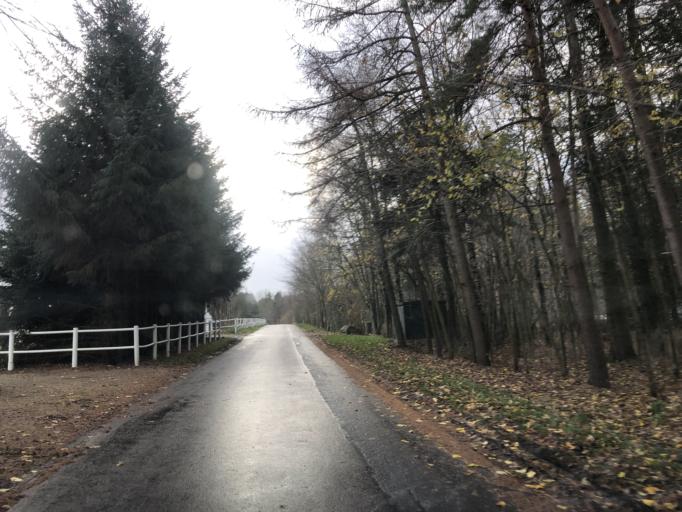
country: DK
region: North Denmark
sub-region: Alborg Kommune
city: Svenstrup
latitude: 56.9336
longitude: 9.8046
